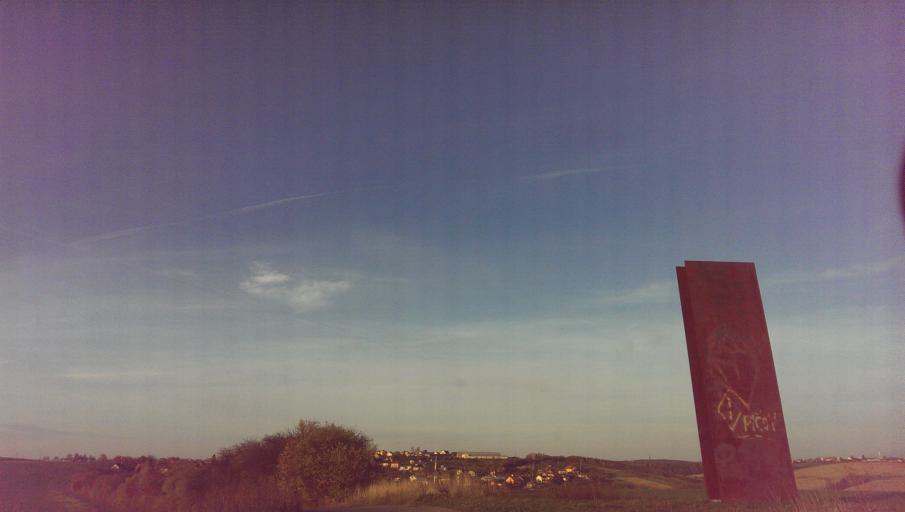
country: CZ
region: Zlin
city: Brezolupy
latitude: 49.1595
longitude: 17.6031
